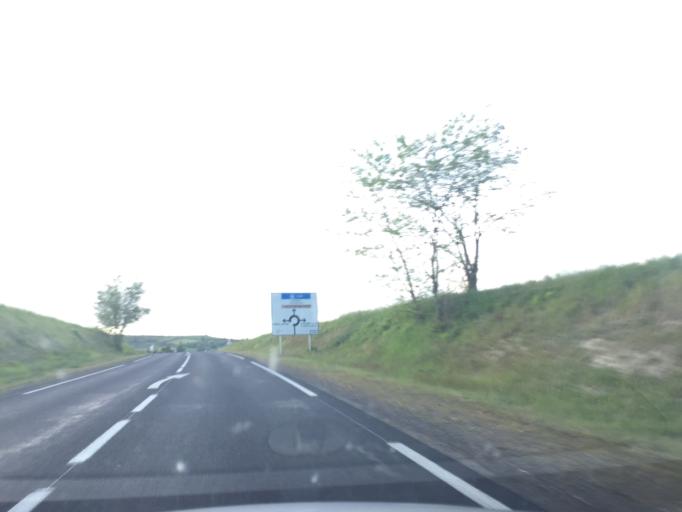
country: FR
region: Auvergne
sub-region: Departement du Puy-de-Dome
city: Chatel-Guyon
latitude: 45.9242
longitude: 3.0852
